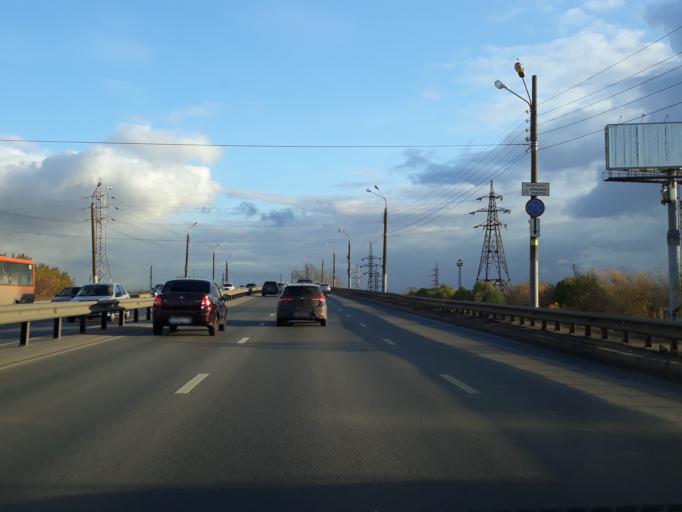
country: RU
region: Nizjnij Novgorod
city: Nizhniy Novgorod
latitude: 56.3088
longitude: 43.9013
